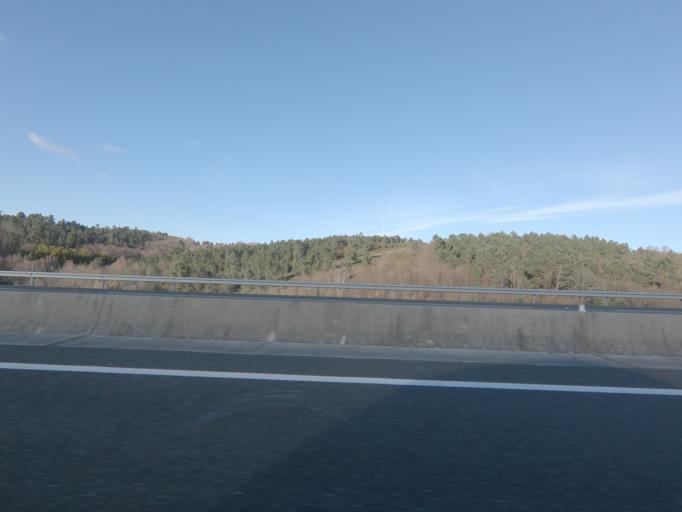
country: ES
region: Galicia
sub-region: Provincia de Pontevedra
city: Lalin
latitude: 42.6004
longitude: -8.0930
